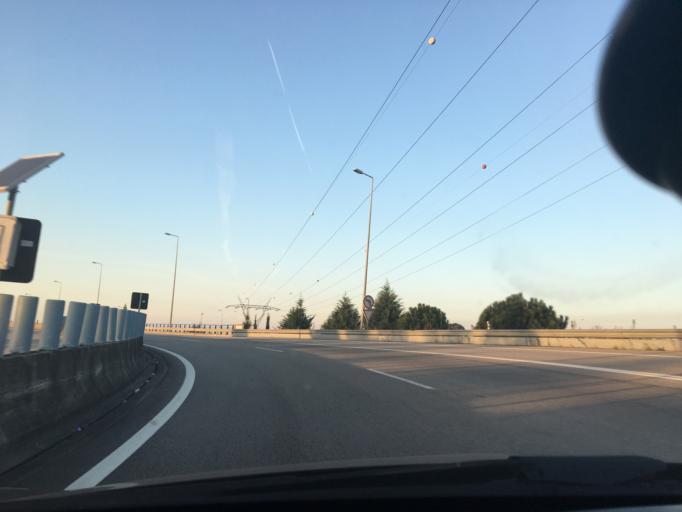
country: PT
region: Porto
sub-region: Matosinhos
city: Senhora da Hora
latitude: 41.2020
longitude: -8.6499
